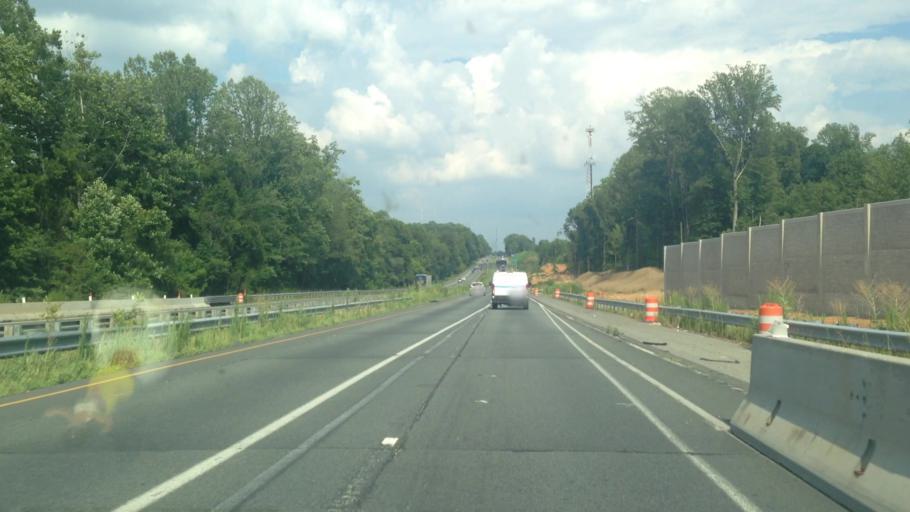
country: US
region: North Carolina
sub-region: Forsyth County
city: Kernersville
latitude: 36.1123
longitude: -80.1219
